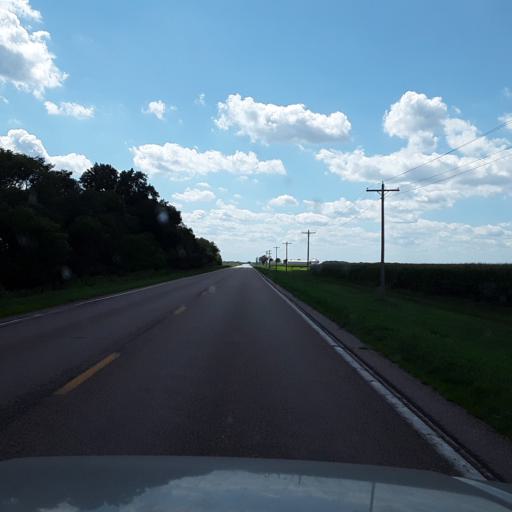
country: US
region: Nebraska
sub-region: Merrick County
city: Central City
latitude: 41.1910
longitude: -98.0251
